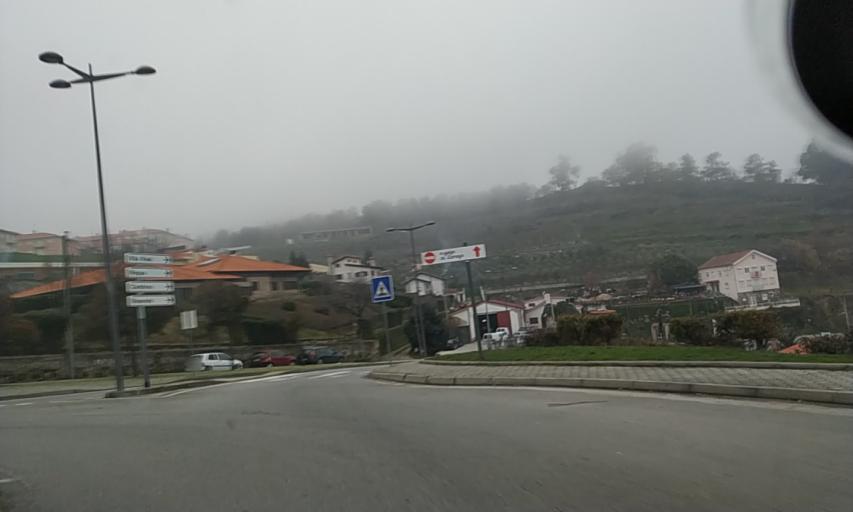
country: PT
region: Viseu
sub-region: Lamego
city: Lamego
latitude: 41.1118
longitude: -7.8050
